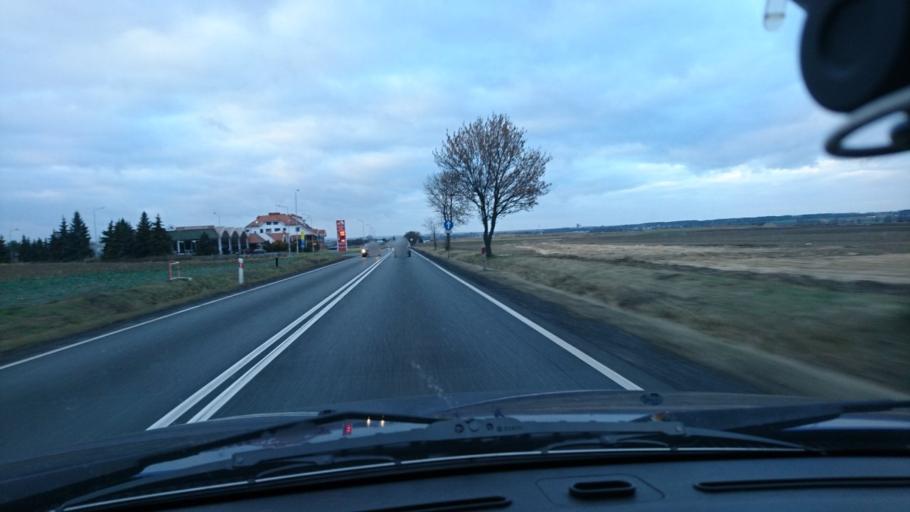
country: PL
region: Greater Poland Voivodeship
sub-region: Powiat kepinski
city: Baranow
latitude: 51.2484
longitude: 18.0168
